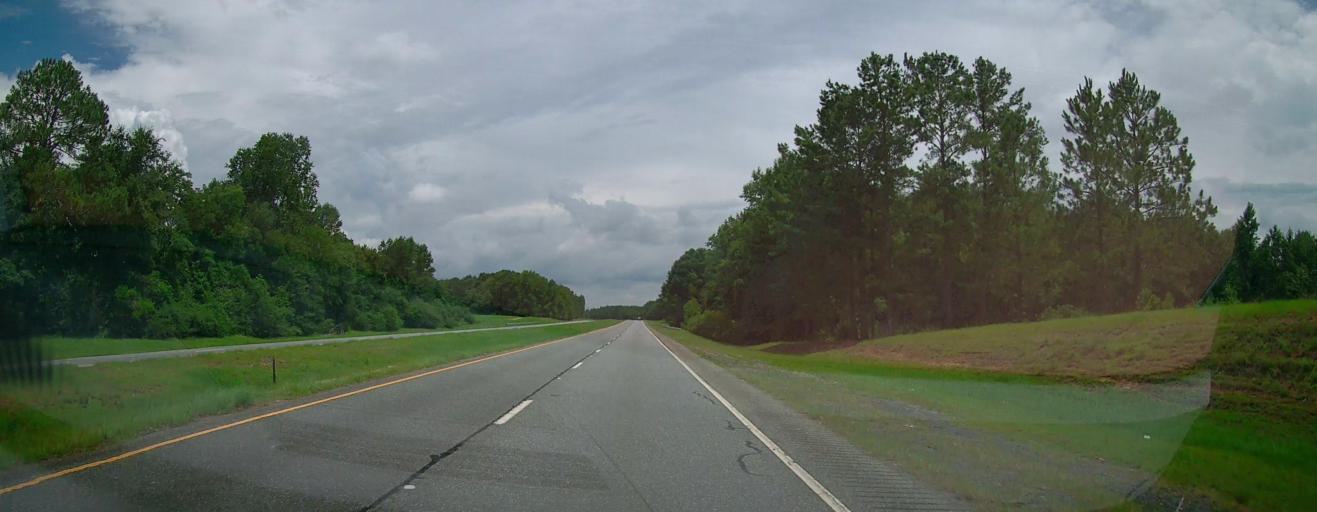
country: US
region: Georgia
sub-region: Dodge County
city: Eastman
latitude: 32.1931
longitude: -83.2073
